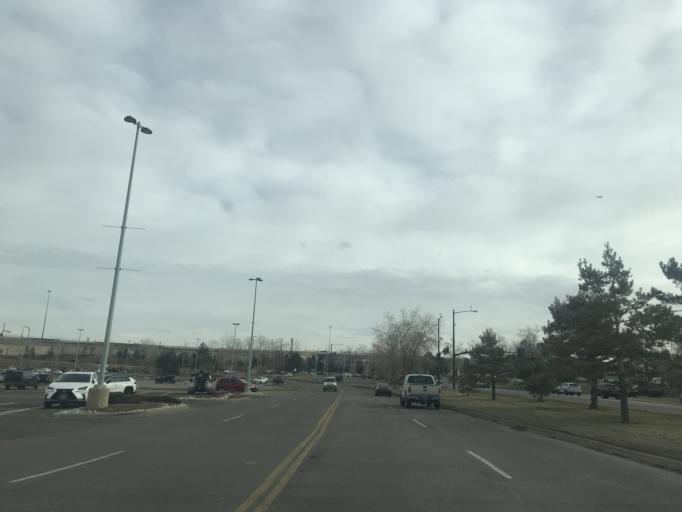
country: US
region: Colorado
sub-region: Adams County
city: Lone Tree
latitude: 39.5596
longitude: -104.8764
